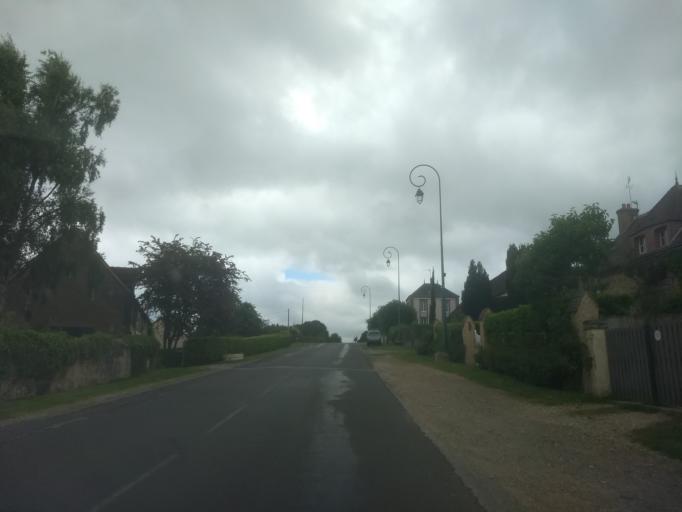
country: FR
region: Lower Normandy
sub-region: Departement de l'Orne
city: Bretoncelles
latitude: 48.4715
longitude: 0.9008
